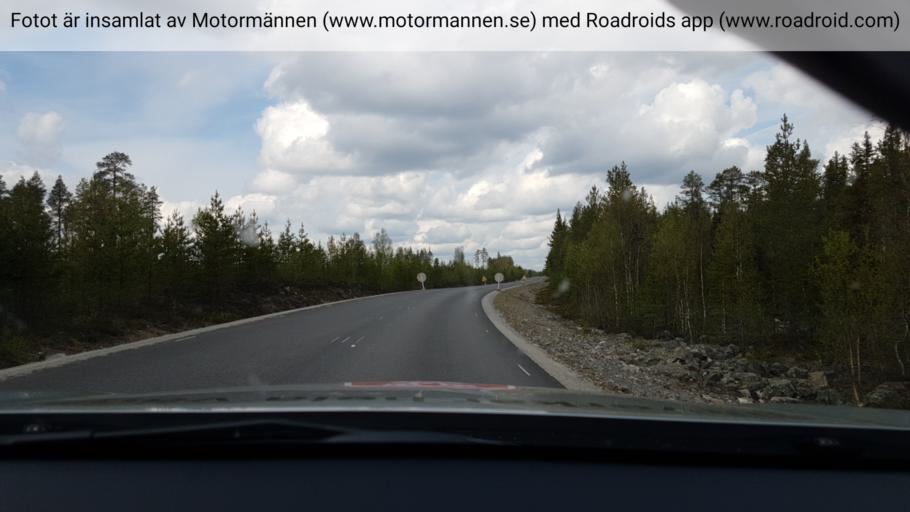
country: SE
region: Vaesterbotten
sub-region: Lycksele Kommun
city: Lycksele
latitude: 63.9795
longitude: 18.4887
